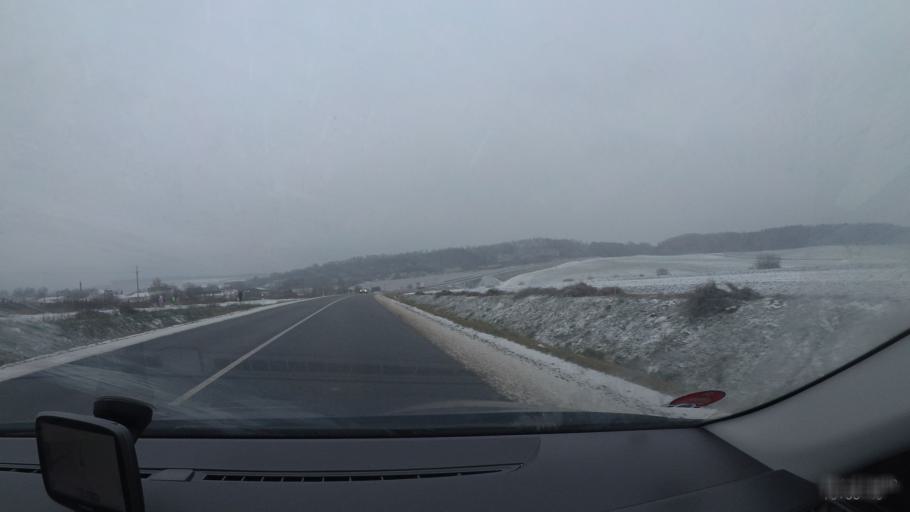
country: CZ
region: Central Bohemia
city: Revnicov
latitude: 50.1835
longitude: 13.8164
